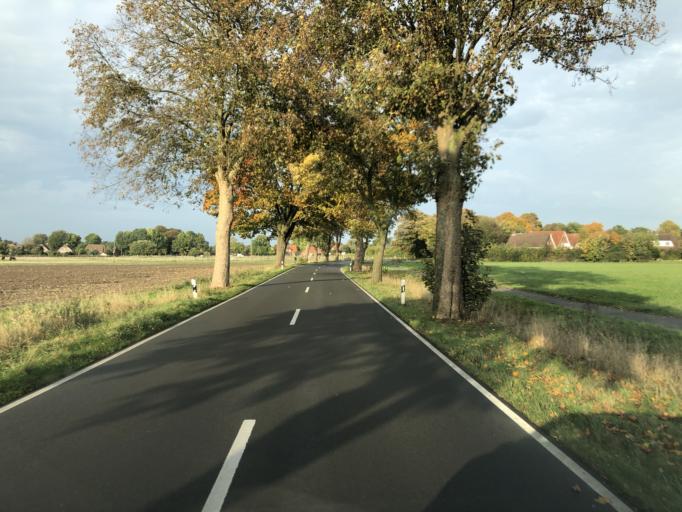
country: DE
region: Lower Saxony
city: Neu Wulmstorf
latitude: 53.4347
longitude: 9.8006
